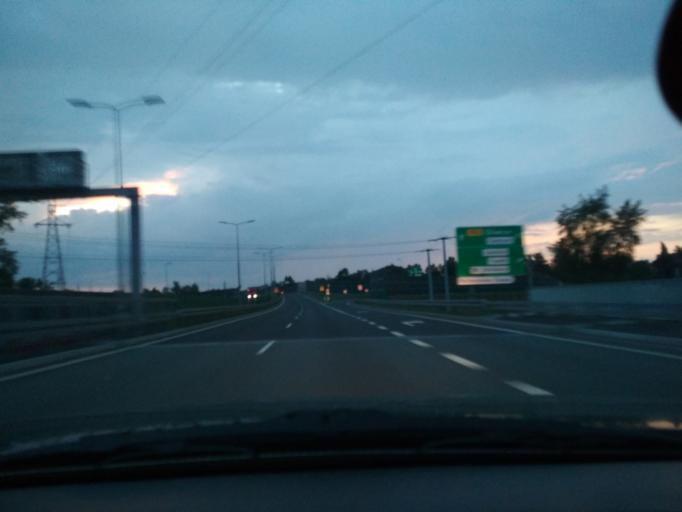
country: PL
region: Silesian Voivodeship
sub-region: Gliwice
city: Gliwice
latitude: 50.2877
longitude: 18.7049
